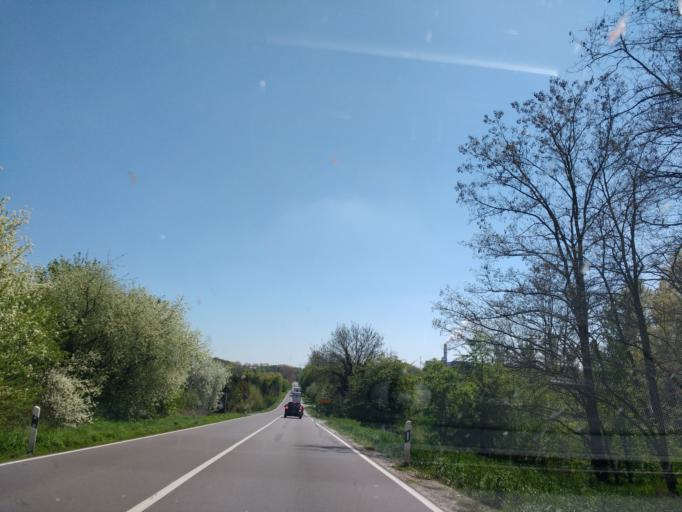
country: DE
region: Saxony-Anhalt
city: Deuben
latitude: 51.1229
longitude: 12.0680
